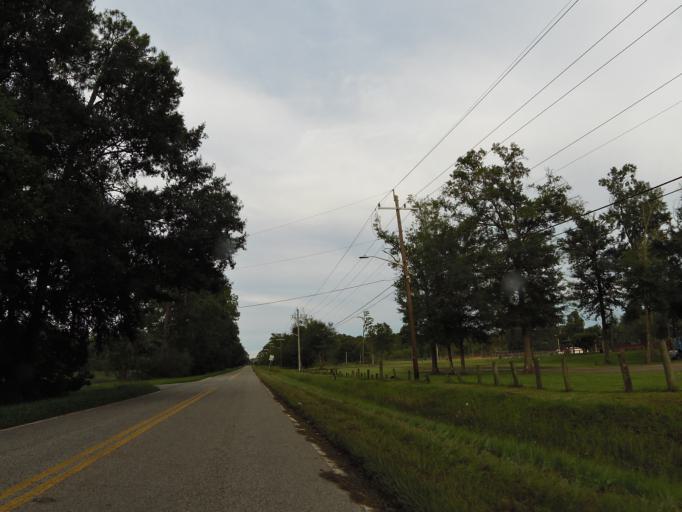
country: US
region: Florida
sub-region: Duval County
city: Jacksonville
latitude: 30.3941
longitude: -81.7506
